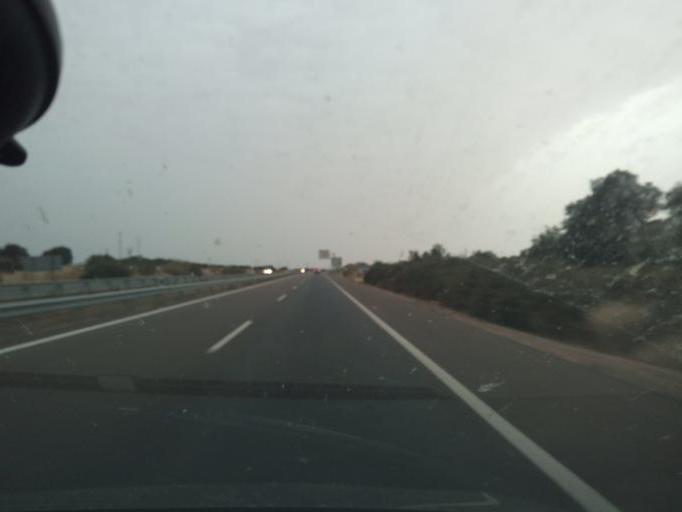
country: ES
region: Extremadura
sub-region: Provincia de Badajoz
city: San Pedro de Merida
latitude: 38.9490
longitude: -6.1720
